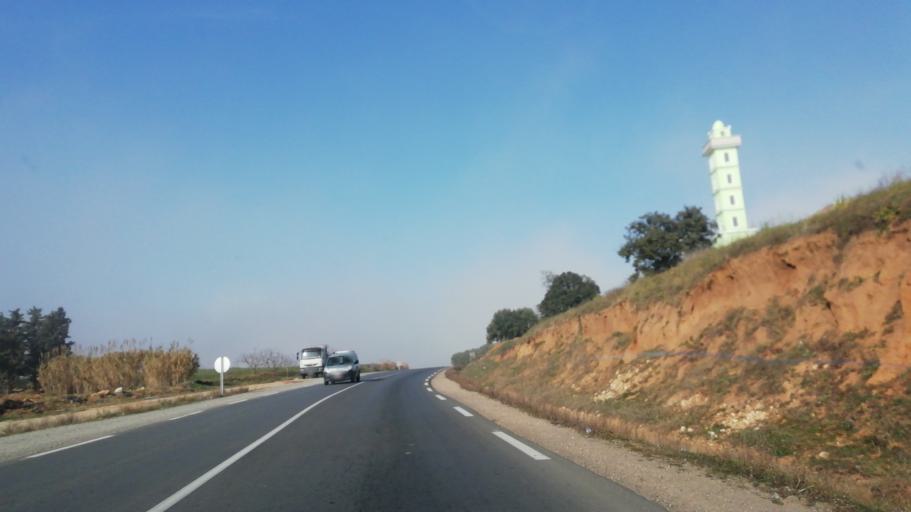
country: DZ
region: Mascara
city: Mascara
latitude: 35.5256
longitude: 0.3476
